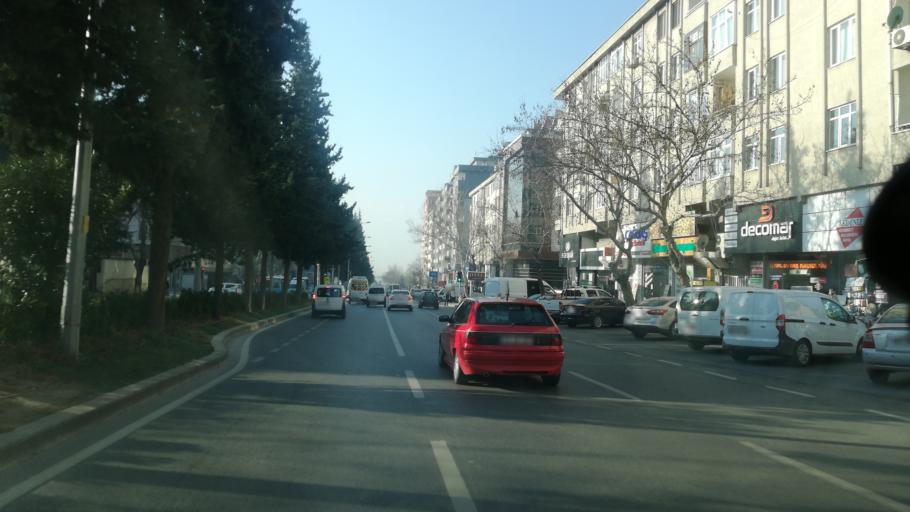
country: TR
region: Kahramanmaras
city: Kahramanmaras
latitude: 37.5732
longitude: 36.9258
